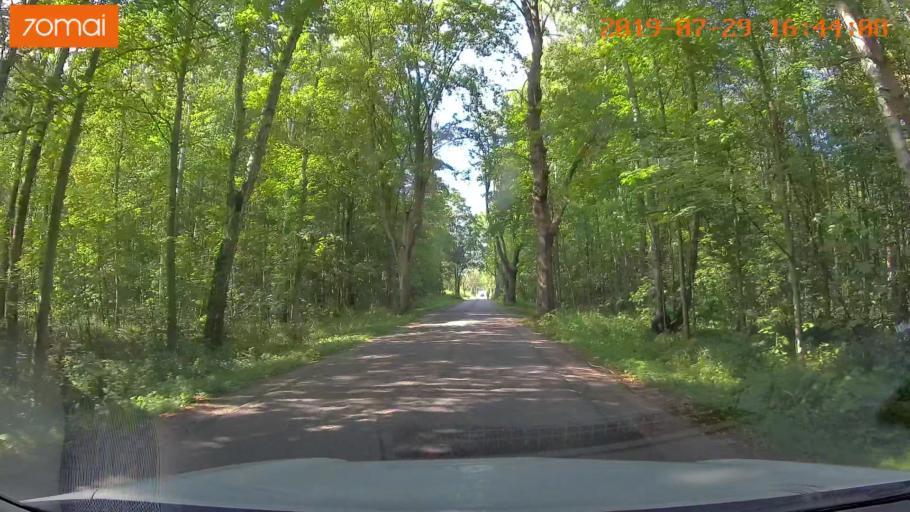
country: RU
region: Kaliningrad
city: Primorsk
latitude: 54.7530
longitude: 20.0895
